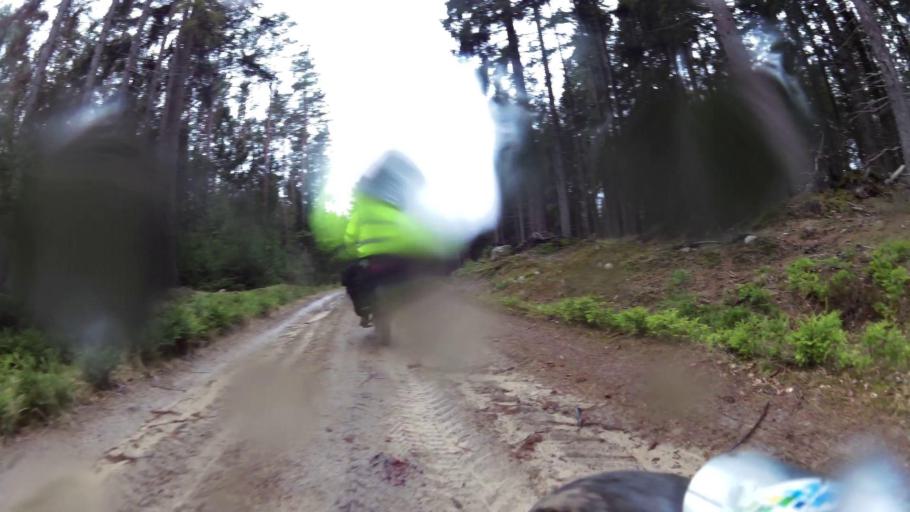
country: PL
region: Pomeranian Voivodeship
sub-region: Powiat bytowski
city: Miastko
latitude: 54.0724
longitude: 17.0878
